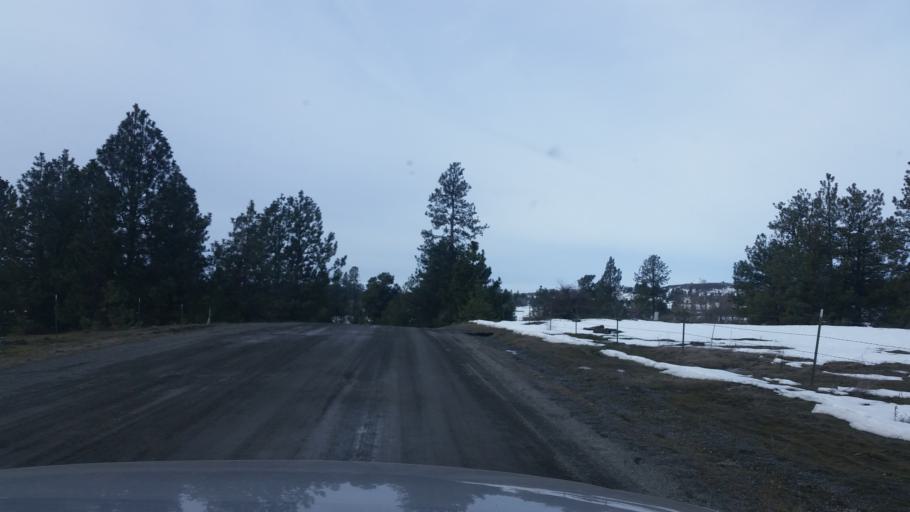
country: US
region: Washington
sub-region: Spokane County
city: Fairchild Air Force Base
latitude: 47.5801
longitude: -117.6427
